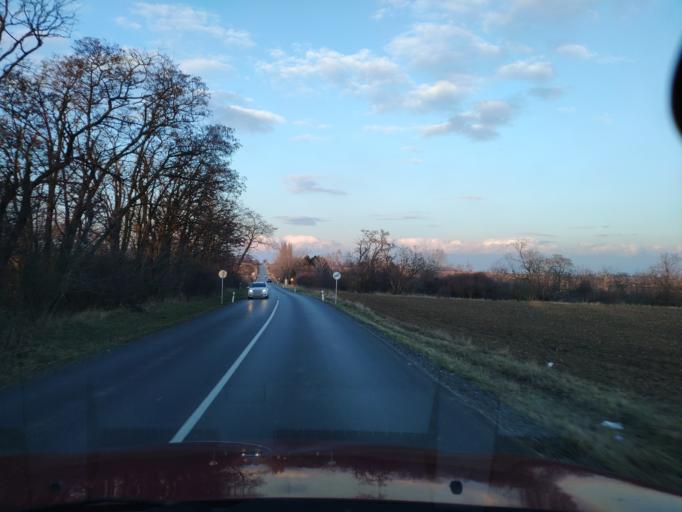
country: SK
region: Nitriansky
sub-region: Okres Nitra
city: Nitra
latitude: 48.2211
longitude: 18.0887
